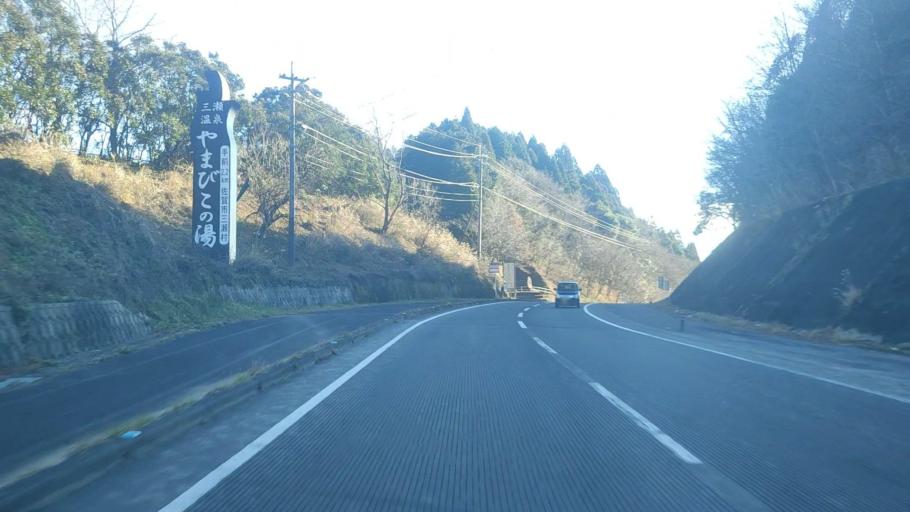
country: JP
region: Saga Prefecture
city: Kanzakimachi-kanzaki
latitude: 33.4048
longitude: 130.2728
